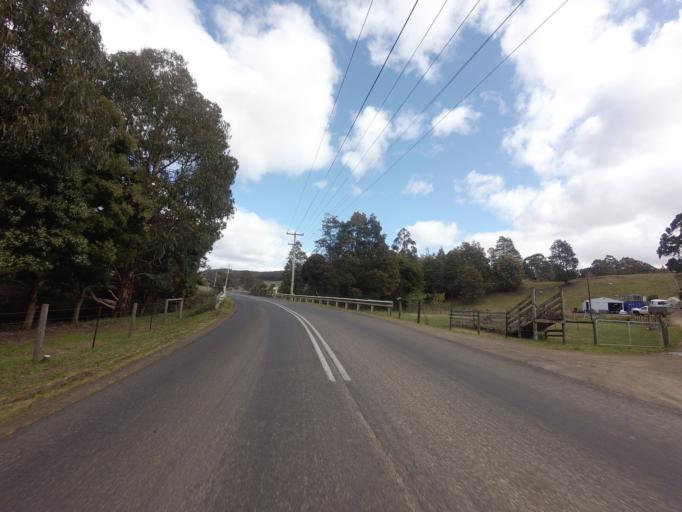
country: AU
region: Tasmania
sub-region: Huon Valley
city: Geeveston
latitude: -43.1755
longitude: 146.9237
